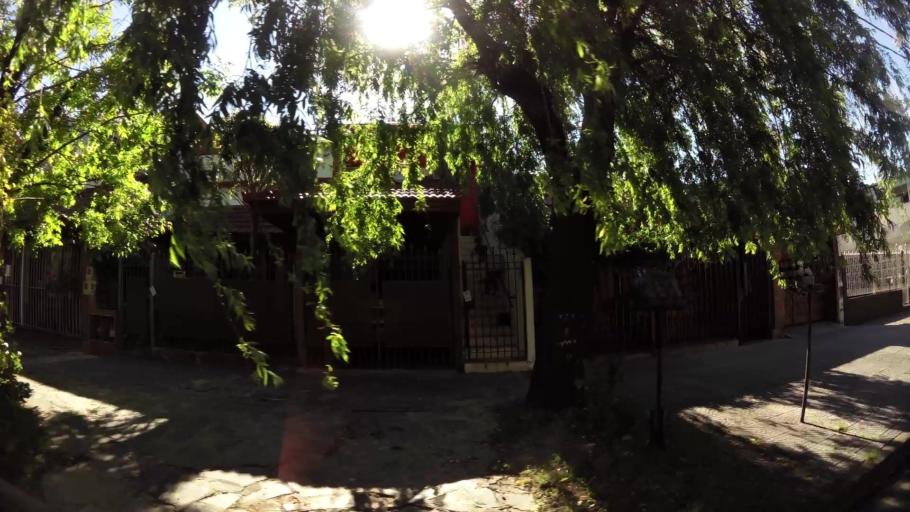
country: AR
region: Buenos Aires
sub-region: Partido de Lomas de Zamora
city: Lomas de Zamora
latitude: -34.7583
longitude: -58.4158
